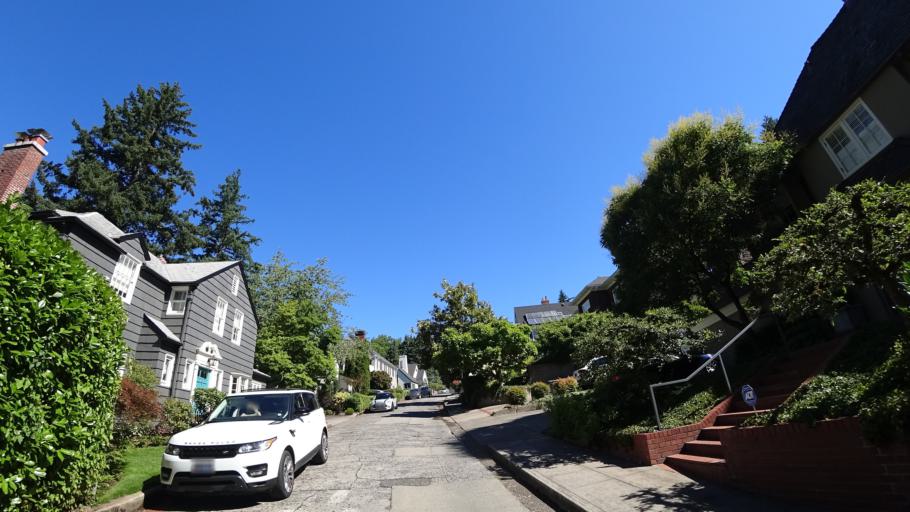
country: US
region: Oregon
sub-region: Multnomah County
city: Portland
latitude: 45.5060
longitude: -122.7034
